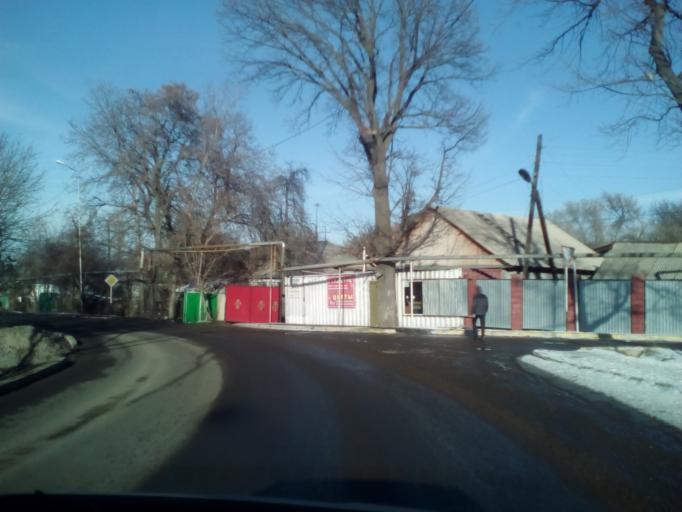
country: KZ
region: Almaty Oblysy
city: Burunday
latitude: 43.1635
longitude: 76.4169
